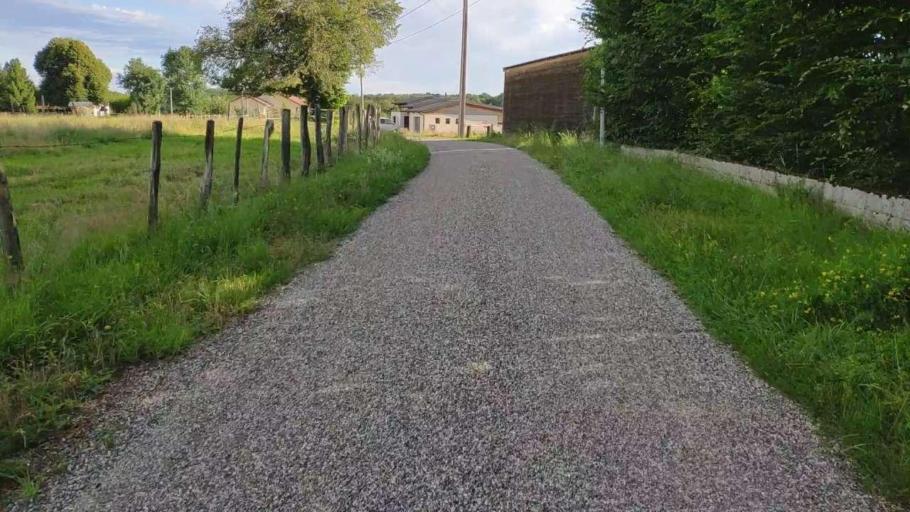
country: FR
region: Franche-Comte
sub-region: Departement du Jura
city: Bletterans
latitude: 46.7996
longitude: 5.4810
